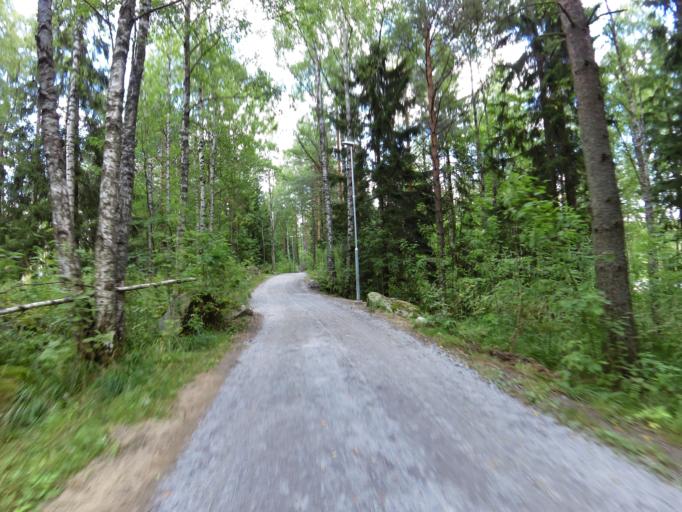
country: FI
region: Pirkanmaa
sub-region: Tampere
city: Yloejaervi
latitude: 61.5088
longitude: 23.6094
